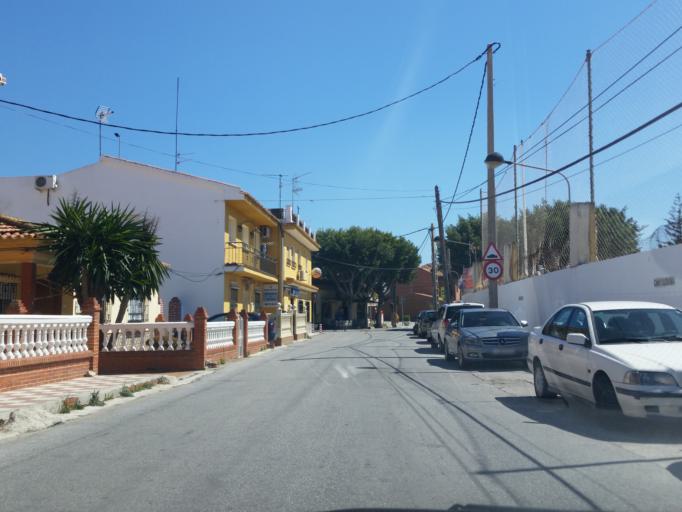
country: ES
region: Andalusia
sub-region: Provincia de Malaga
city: Torremolinos
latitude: 36.6678
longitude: -4.4757
